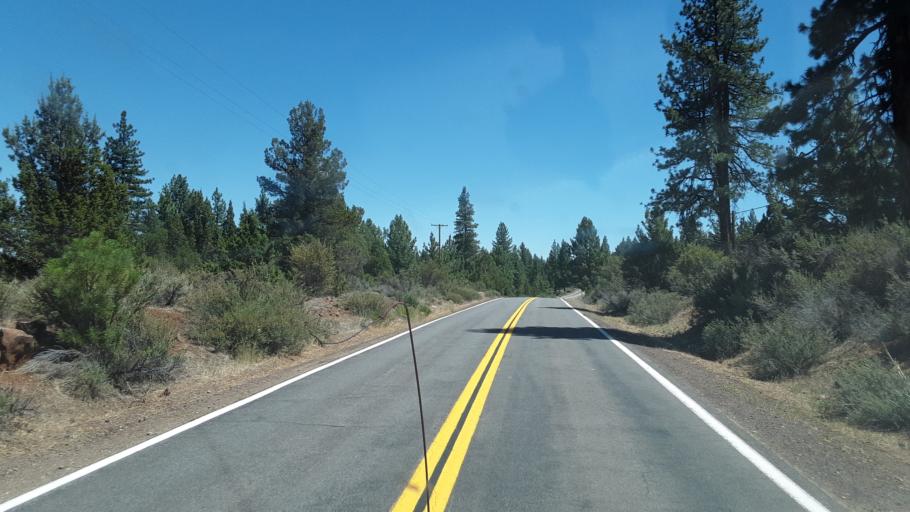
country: US
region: California
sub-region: Lassen County
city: Susanville
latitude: 40.5120
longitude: -120.5749
